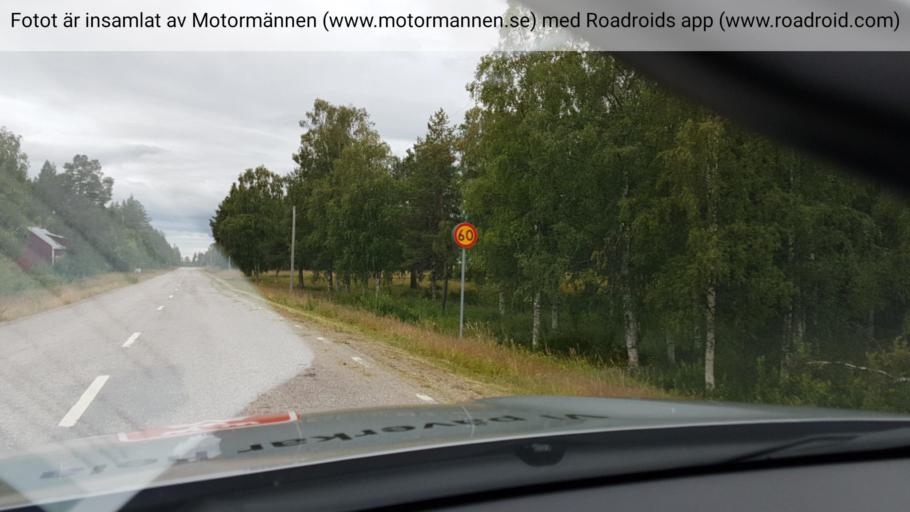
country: SE
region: Norrbotten
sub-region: Overkalix Kommun
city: OEverkalix
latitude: 66.7858
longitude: 22.9138
